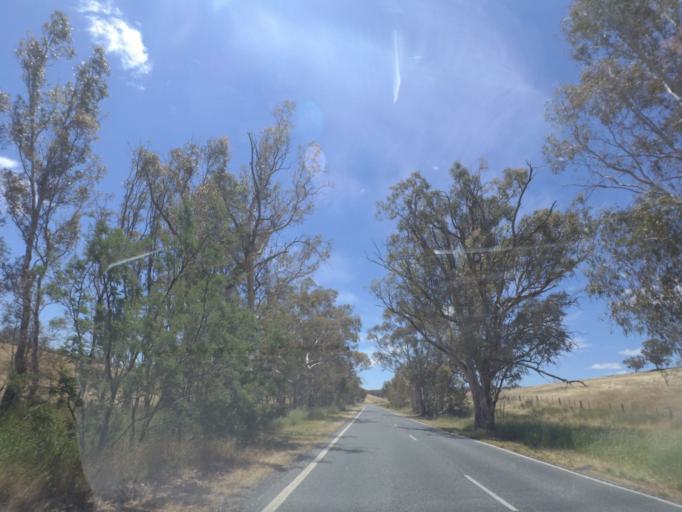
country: AU
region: Victoria
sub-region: Mount Alexander
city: Castlemaine
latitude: -37.1946
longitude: 144.1478
